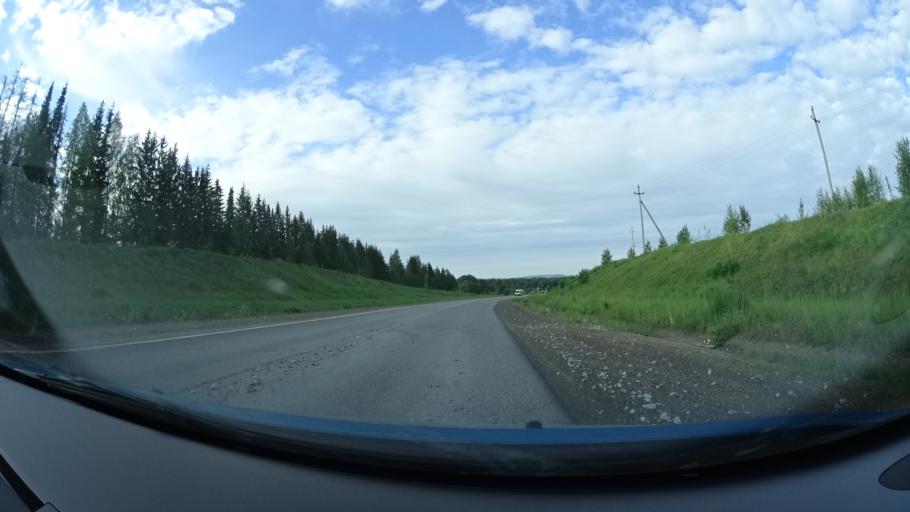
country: RU
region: Perm
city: Osa
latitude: 57.4002
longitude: 55.6236
